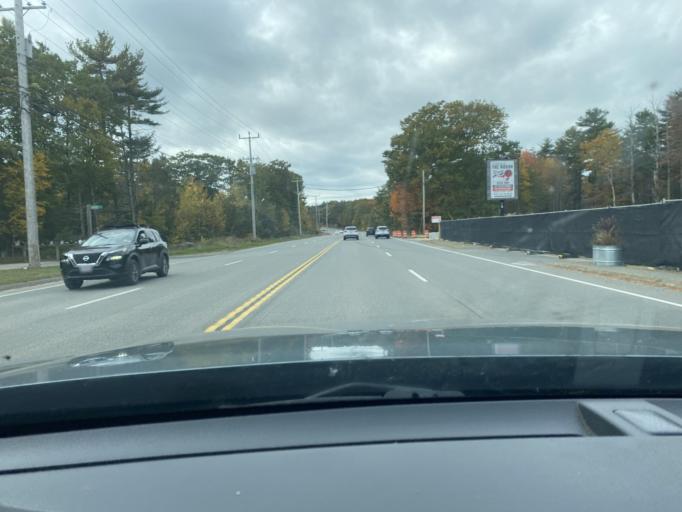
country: US
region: Maine
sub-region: York County
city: Cape Neddick
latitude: 43.1776
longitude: -70.6317
